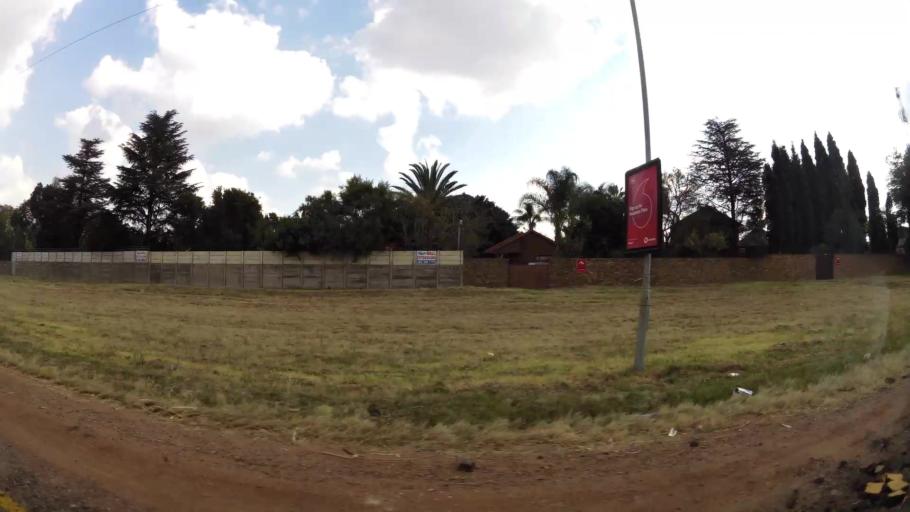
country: ZA
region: Gauteng
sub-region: City of Tshwane Metropolitan Municipality
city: Centurion
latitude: -25.8246
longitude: 28.2556
